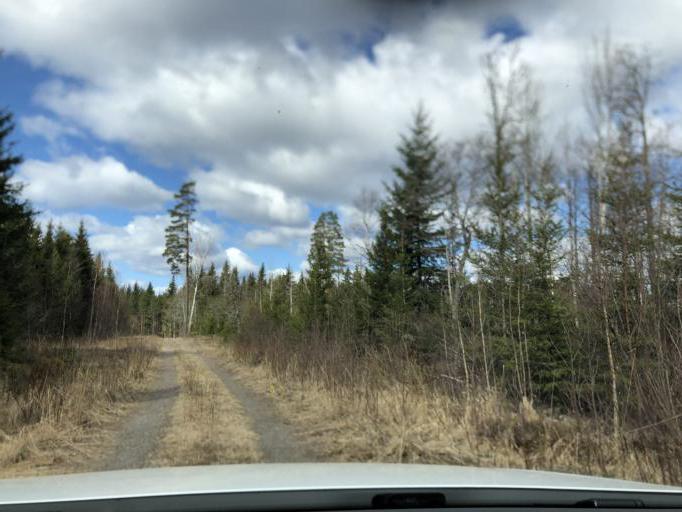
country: SE
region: Uppsala
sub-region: Tierps Kommun
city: Tierp
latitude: 60.3319
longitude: 17.3362
